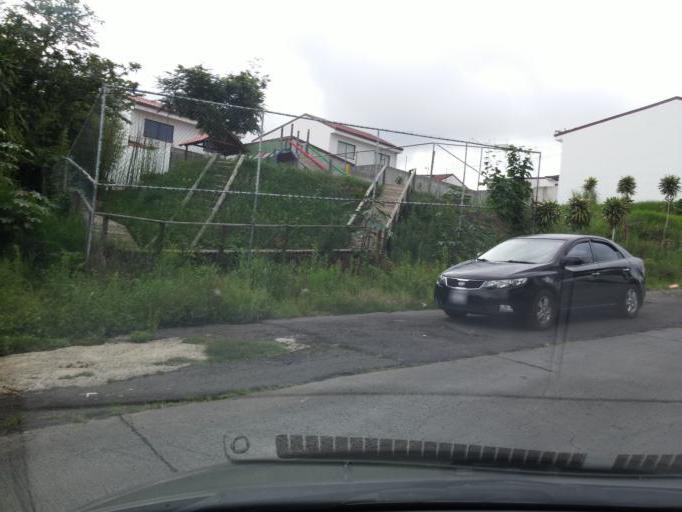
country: CR
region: Heredia
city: Mercedes
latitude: 10.0215
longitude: -84.1301
